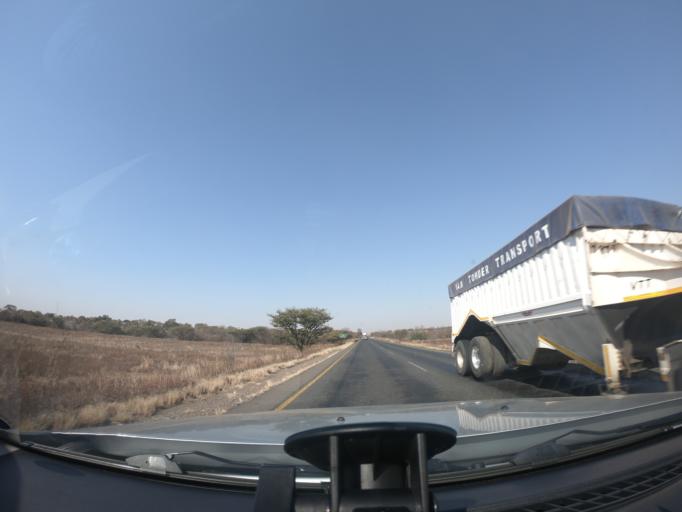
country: ZA
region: KwaZulu-Natal
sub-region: uThukela District Municipality
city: Ladysmith
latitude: -28.7395
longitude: 29.8180
